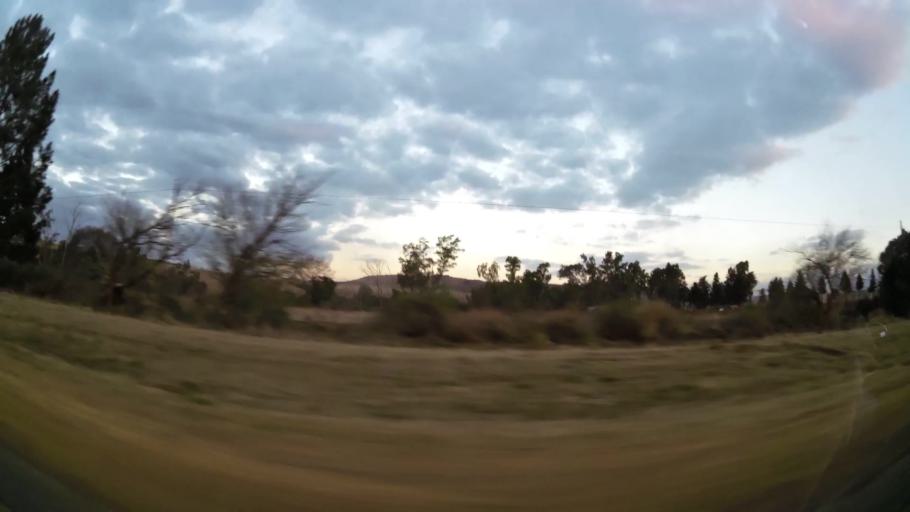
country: ZA
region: Gauteng
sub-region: West Rand District Municipality
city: Krugersdorp
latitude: -26.0418
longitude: 27.7195
